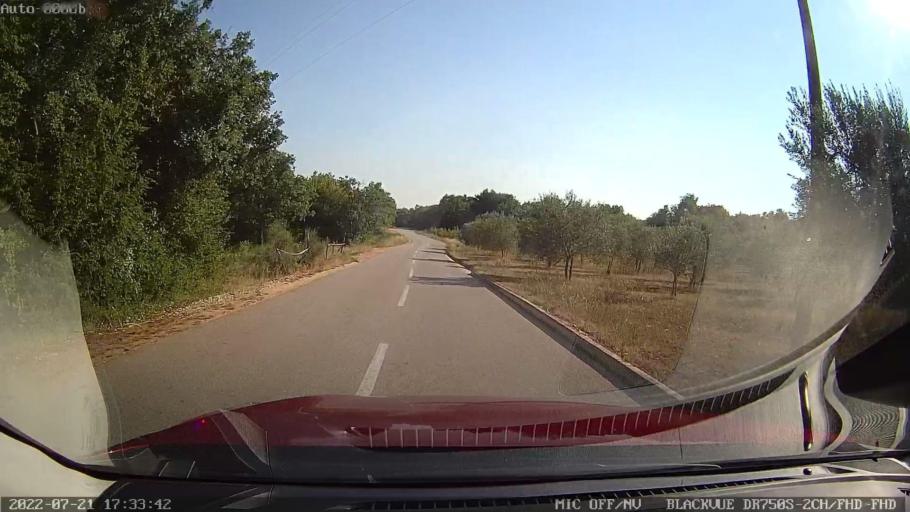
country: HR
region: Istarska
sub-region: Grad Rovinj
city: Rovinj
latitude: 45.1703
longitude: 13.7460
